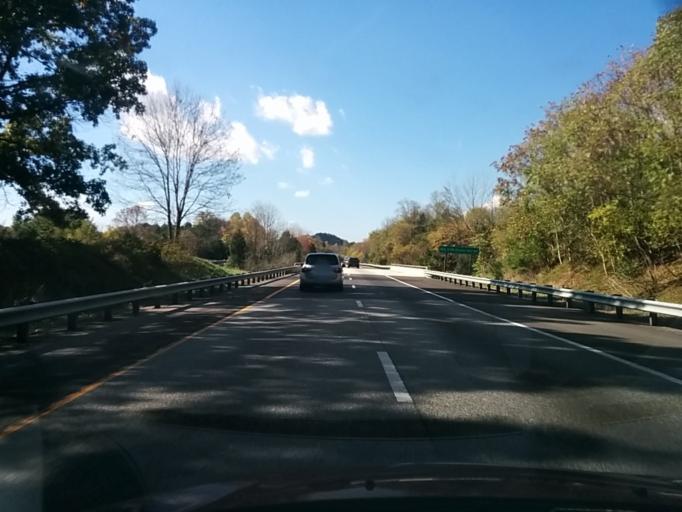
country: US
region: Virginia
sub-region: Botetourt County
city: Fincastle
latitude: 37.4499
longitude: -79.8541
